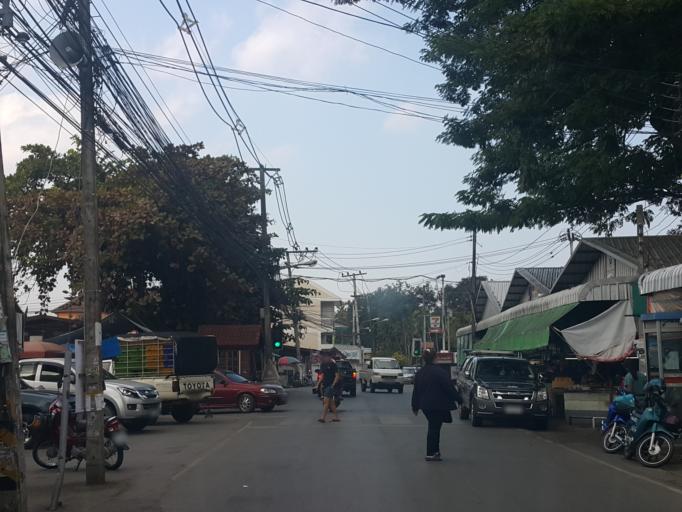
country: TH
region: Chiang Mai
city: Chiang Mai
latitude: 18.8368
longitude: 98.9894
